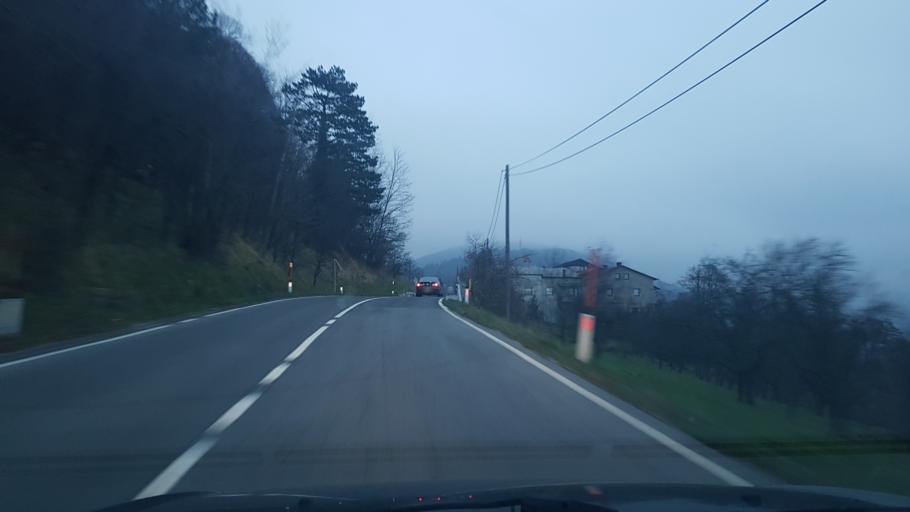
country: SI
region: Vipava
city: Vipava
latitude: 45.8812
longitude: 13.9957
